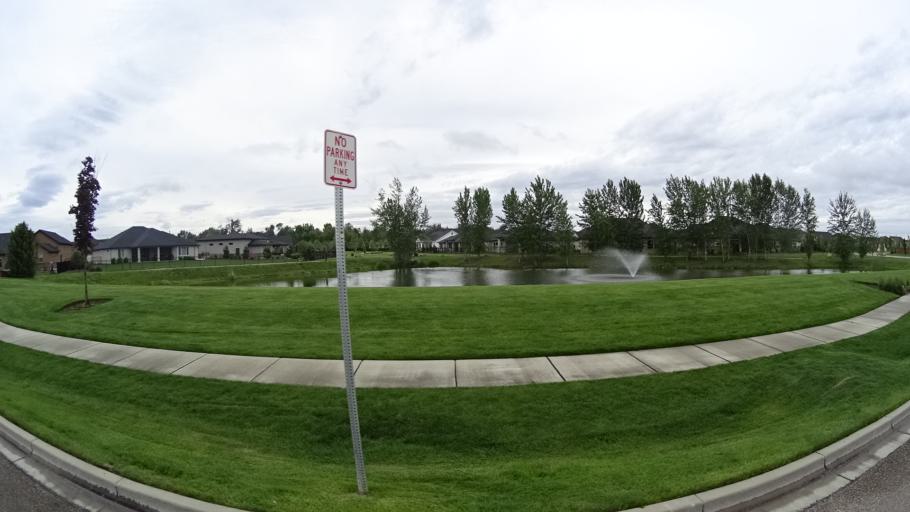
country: US
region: Idaho
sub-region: Ada County
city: Star
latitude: 43.6882
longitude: -116.4760
